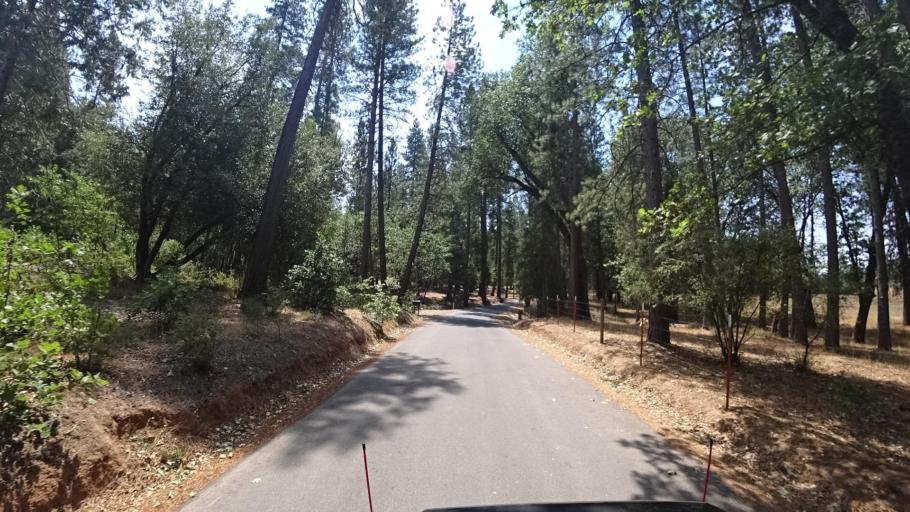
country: US
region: California
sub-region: Mariposa County
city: Midpines
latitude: 37.7242
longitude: -120.0901
